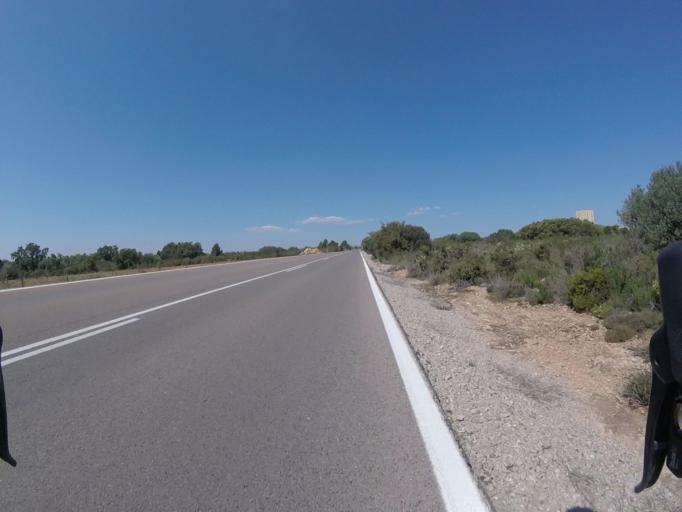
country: ES
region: Valencia
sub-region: Provincia de Castello
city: Benlloch
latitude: 40.2027
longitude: 0.0043
